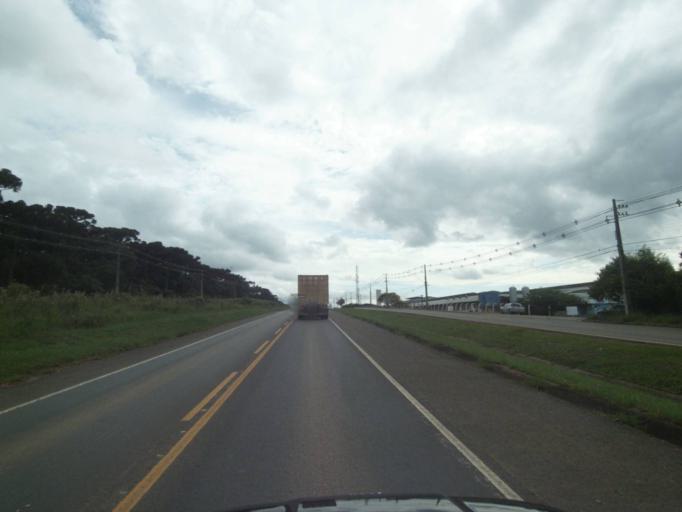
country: BR
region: Parana
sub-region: Telemaco Borba
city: Telemaco Borba
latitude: -24.3738
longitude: -50.6641
